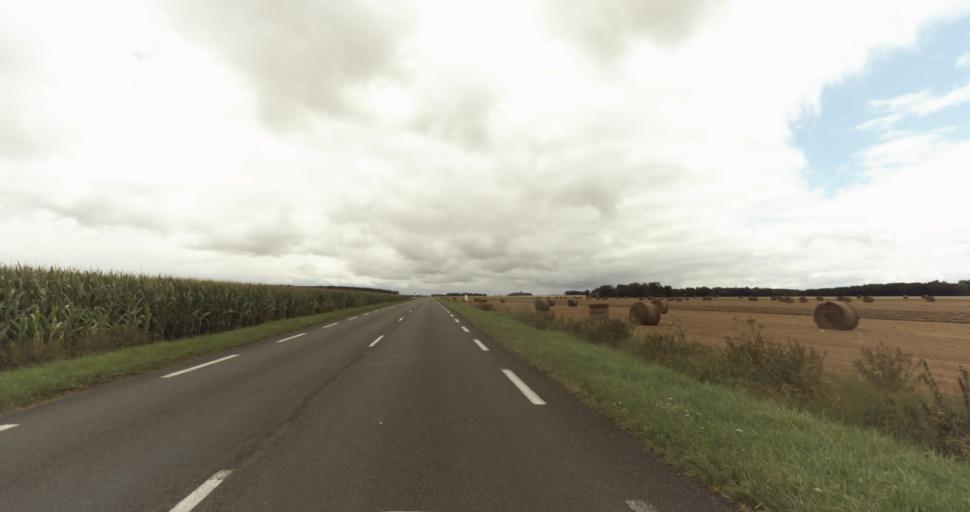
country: FR
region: Haute-Normandie
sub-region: Departement de l'Eure
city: Arnieres-sur-Iton
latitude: 48.9485
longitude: 1.1630
